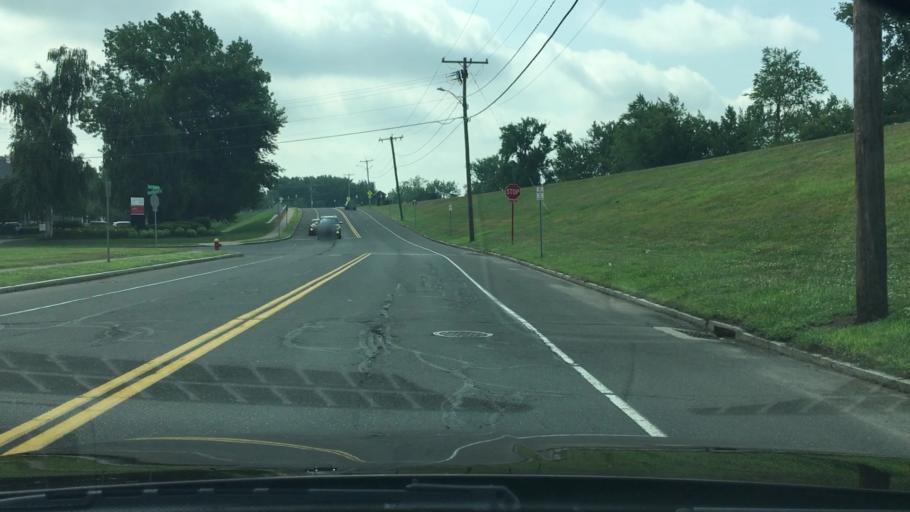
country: US
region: Connecticut
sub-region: Hartford County
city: Hartford
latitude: 41.7624
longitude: -72.6619
